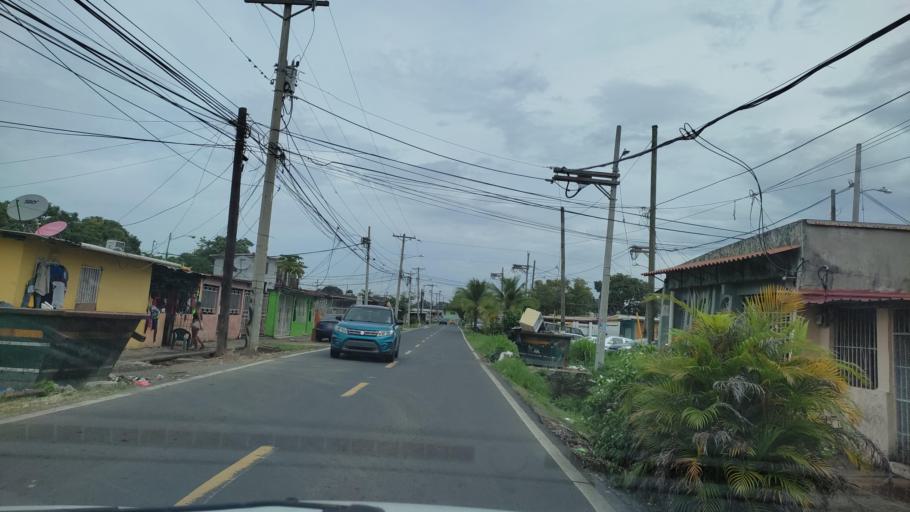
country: PA
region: Panama
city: San Miguelito
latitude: 9.0491
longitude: -79.4326
